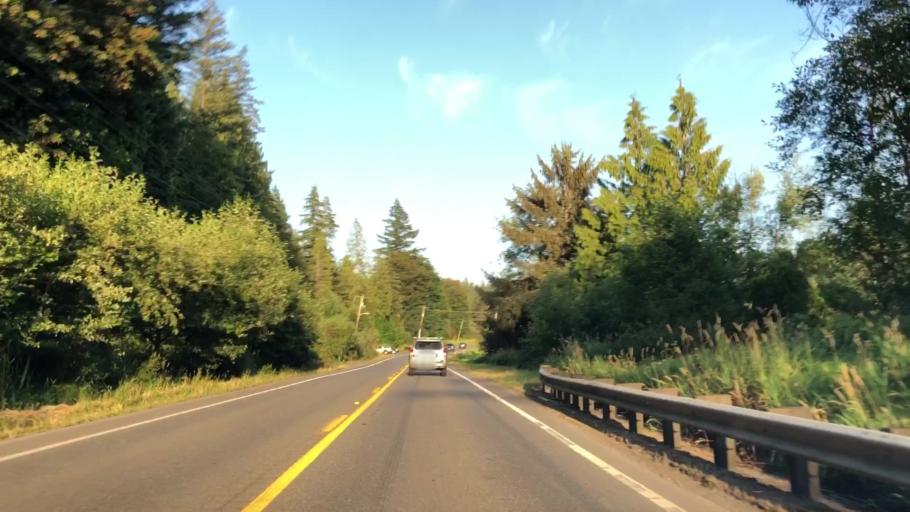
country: US
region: Washington
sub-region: King County
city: Union Hill-Novelty Hill
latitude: 47.6425
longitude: -122.0168
